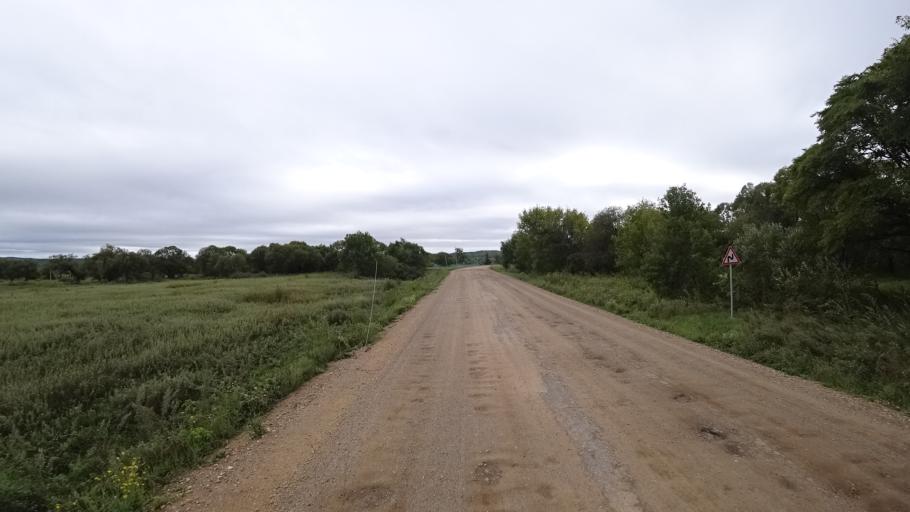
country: RU
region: Primorskiy
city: Rettikhovka
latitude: 44.1328
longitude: 132.6460
